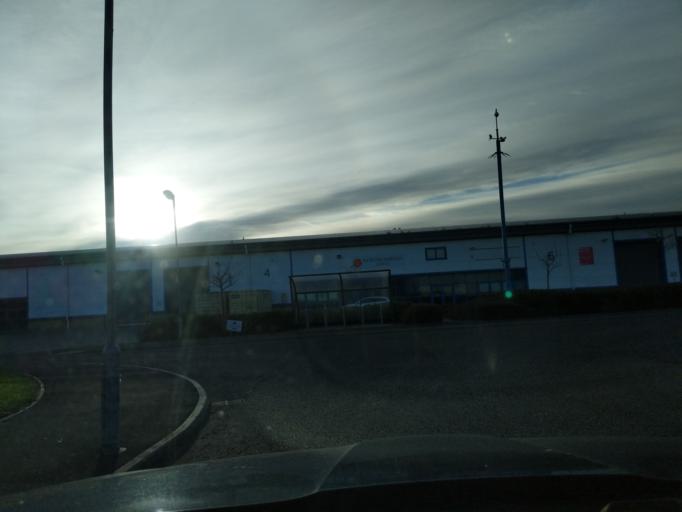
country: GB
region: England
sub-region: Northumberland
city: Newbiggin-by-the-Sea
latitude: 55.1699
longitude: -1.5388
